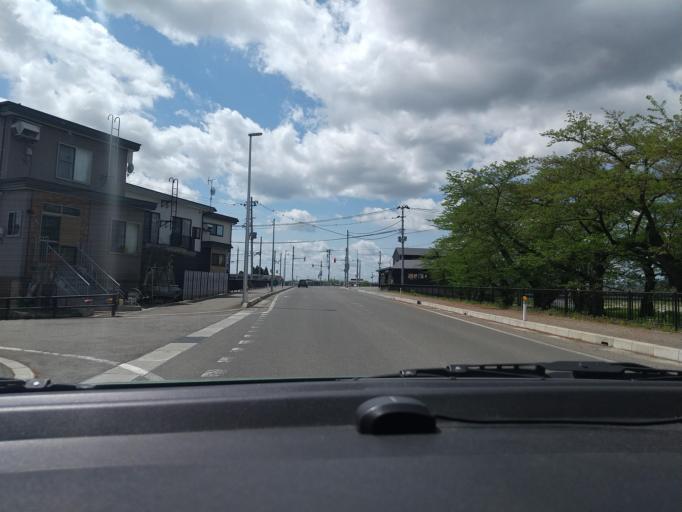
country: JP
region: Akita
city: Kakunodatemachi
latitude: 39.5923
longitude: 140.5601
